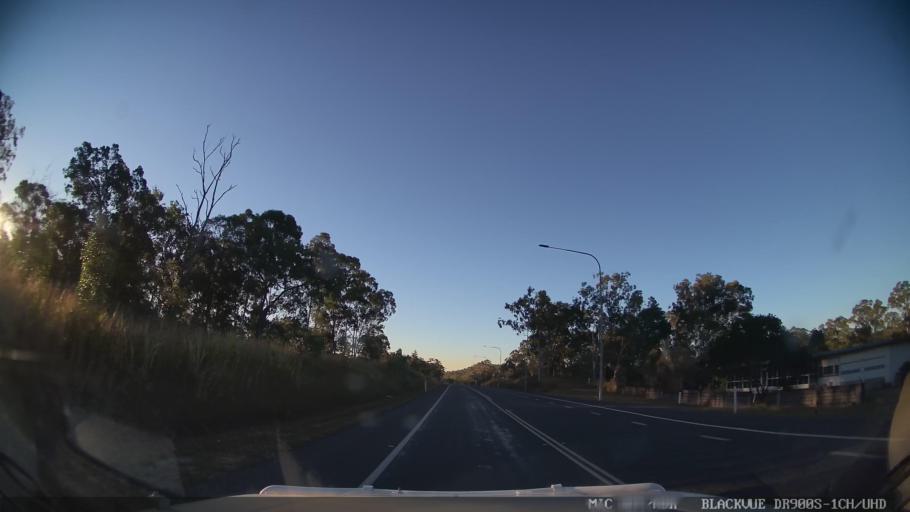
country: AU
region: Queensland
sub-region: Gladstone
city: Toolooa
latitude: -23.9553
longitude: 151.2203
